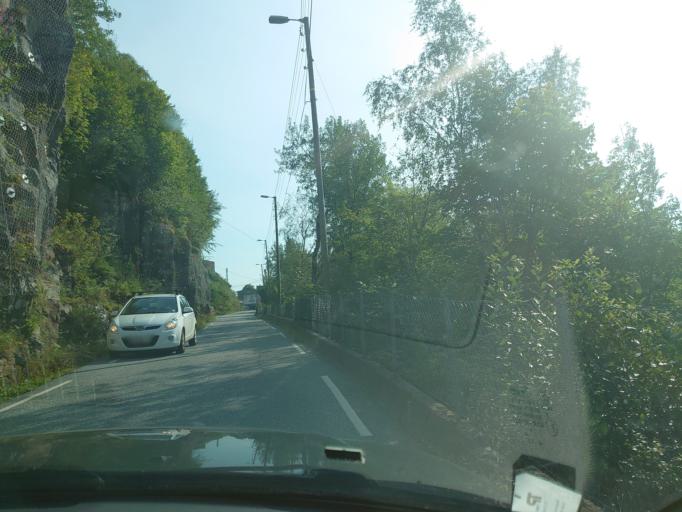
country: NO
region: Hordaland
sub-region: Bergen
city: Ytrebygda
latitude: 60.3289
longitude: 5.2813
